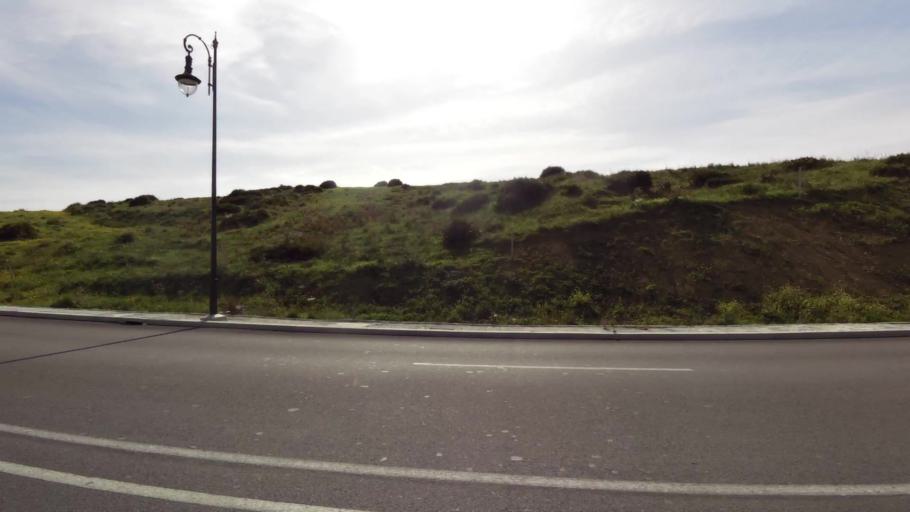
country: MA
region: Tanger-Tetouan
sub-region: Tanger-Assilah
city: Tangier
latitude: 35.7074
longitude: -5.7821
